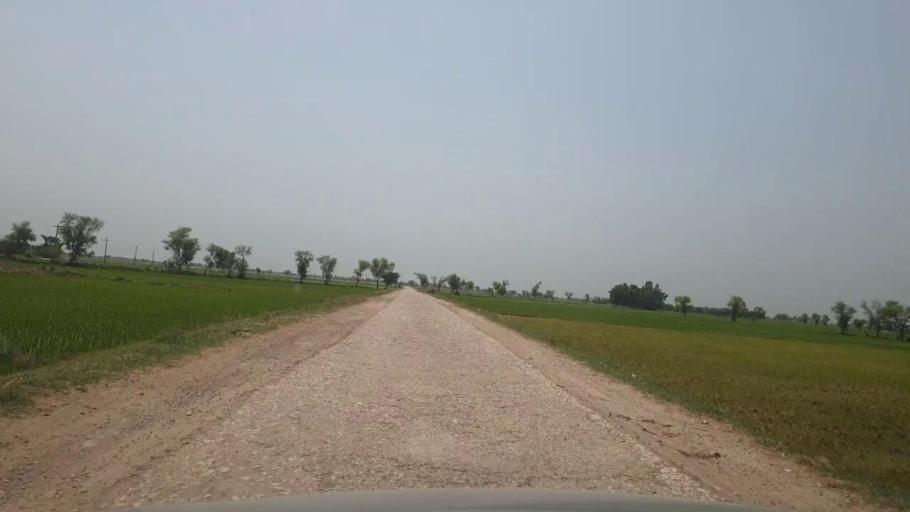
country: PK
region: Sindh
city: Garhi Yasin
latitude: 27.9227
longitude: 68.4040
